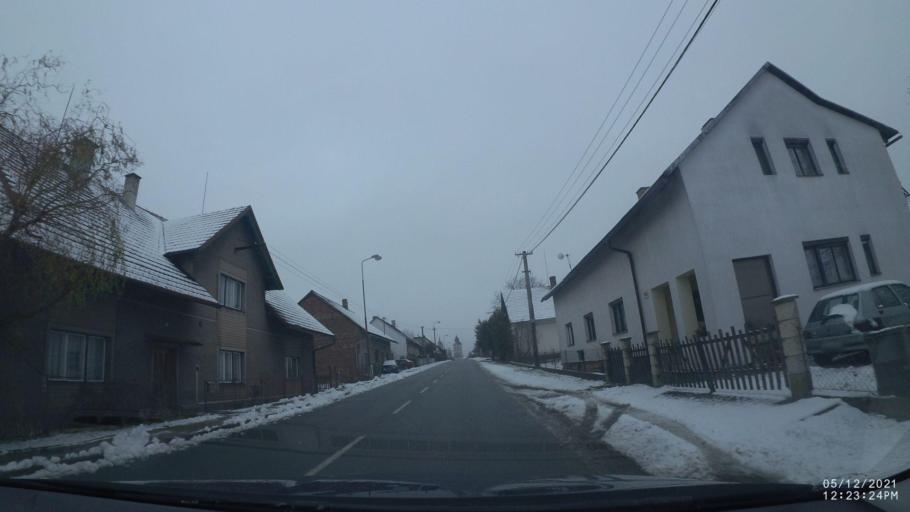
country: CZ
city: Ceske Mezirici
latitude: 50.3121
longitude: 16.0807
